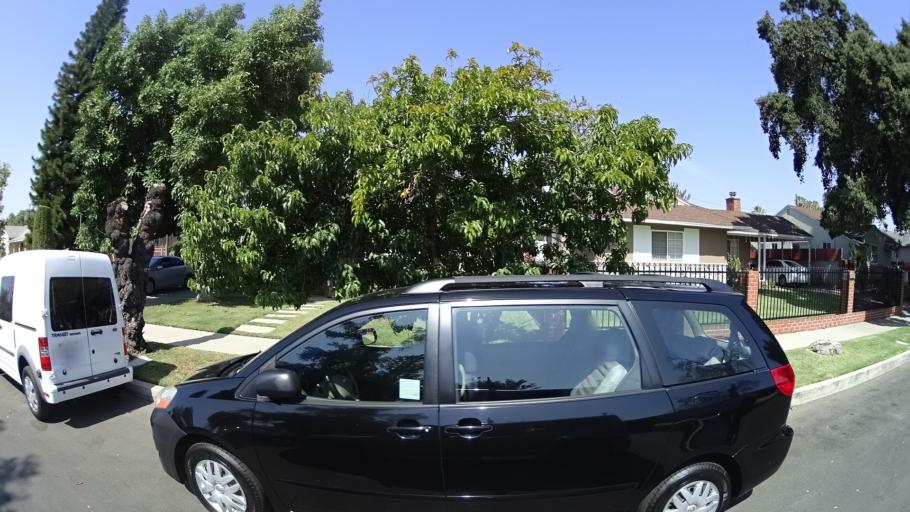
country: US
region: California
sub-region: Los Angeles County
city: Van Nuys
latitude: 34.1985
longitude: -118.4552
